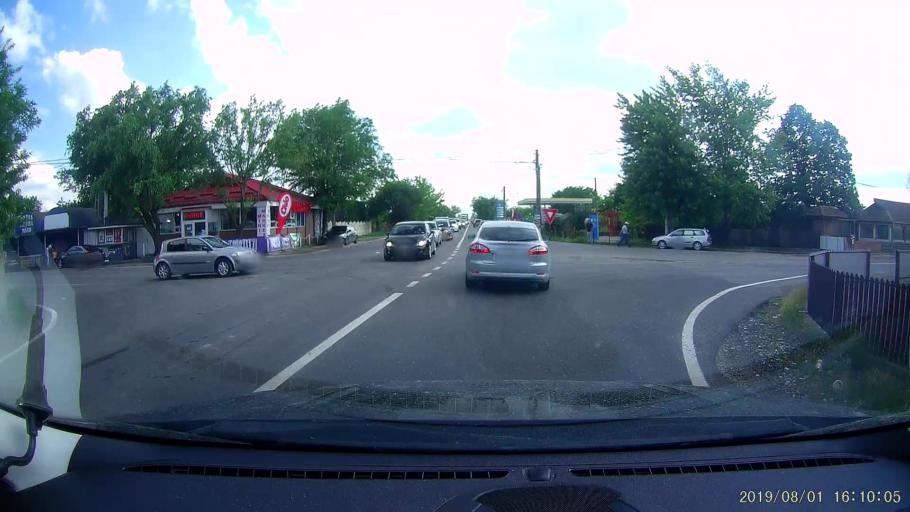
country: RO
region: Calarasi
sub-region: Comuna Dragalina
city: Drajna Noua
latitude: 44.4270
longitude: 27.3764
